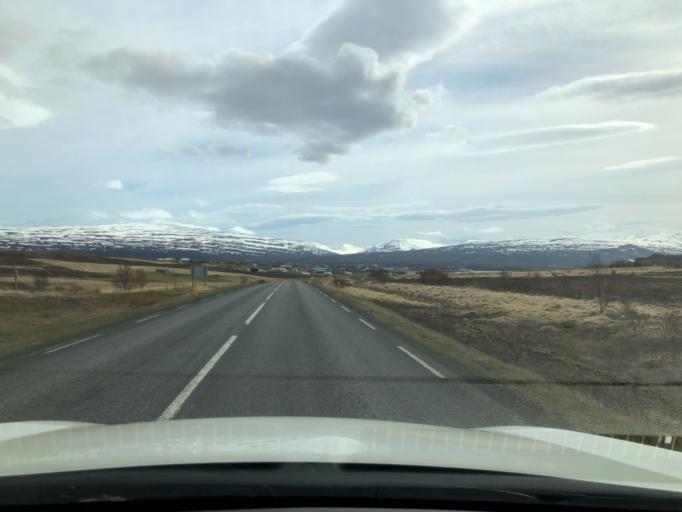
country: IS
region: East
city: Egilsstadir
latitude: 65.2956
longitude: -14.4422
